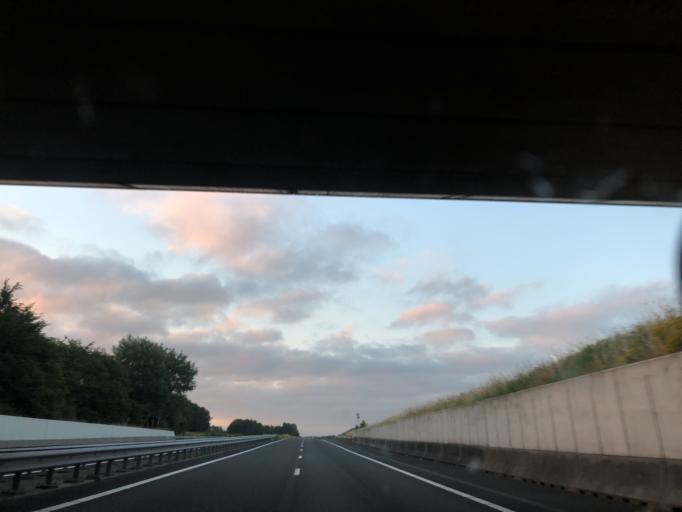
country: NL
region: Groningen
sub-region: Gemeente  Oldambt
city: Winschoten
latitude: 53.1554
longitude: 7.0549
